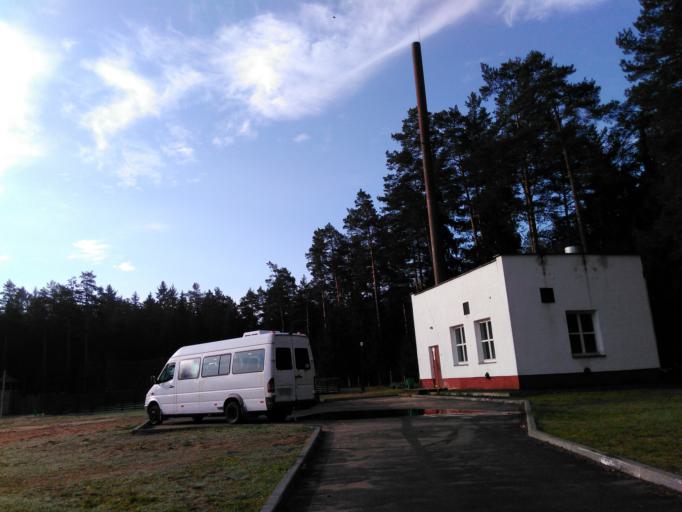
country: BY
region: Minsk
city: Rakaw
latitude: 53.9694
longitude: 27.0147
